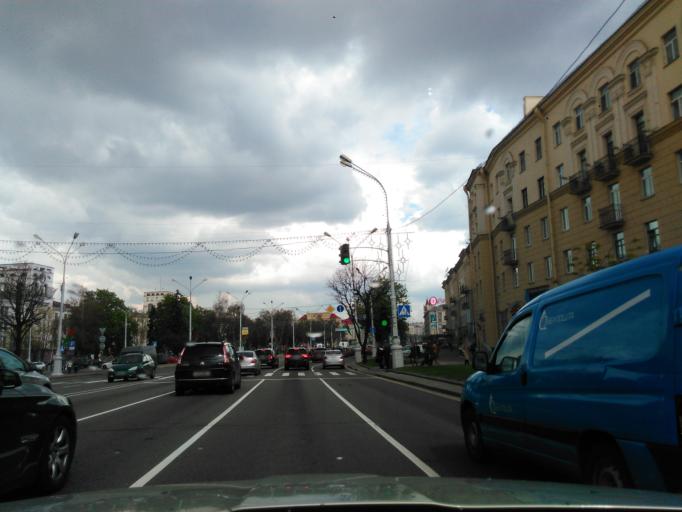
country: BY
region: Minsk
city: Minsk
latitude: 53.9136
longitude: 27.5809
